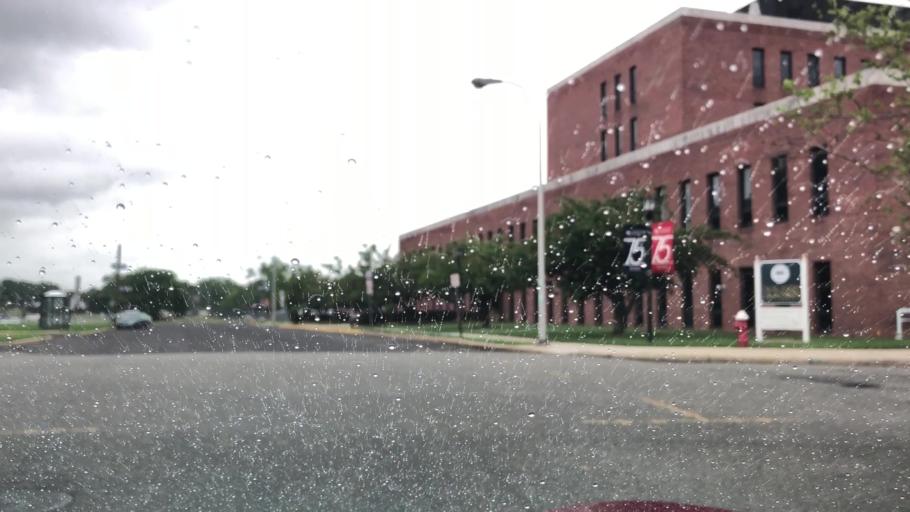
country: US
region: New Jersey
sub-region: Bergen County
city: Hackensack
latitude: 40.8974
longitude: -74.0339
